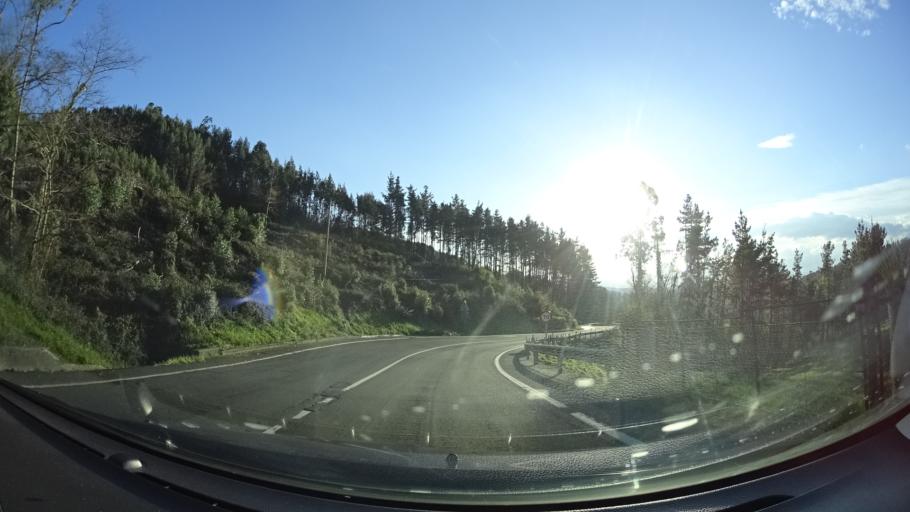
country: ES
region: Basque Country
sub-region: Bizkaia
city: Mungia
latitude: 43.3801
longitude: -2.7912
